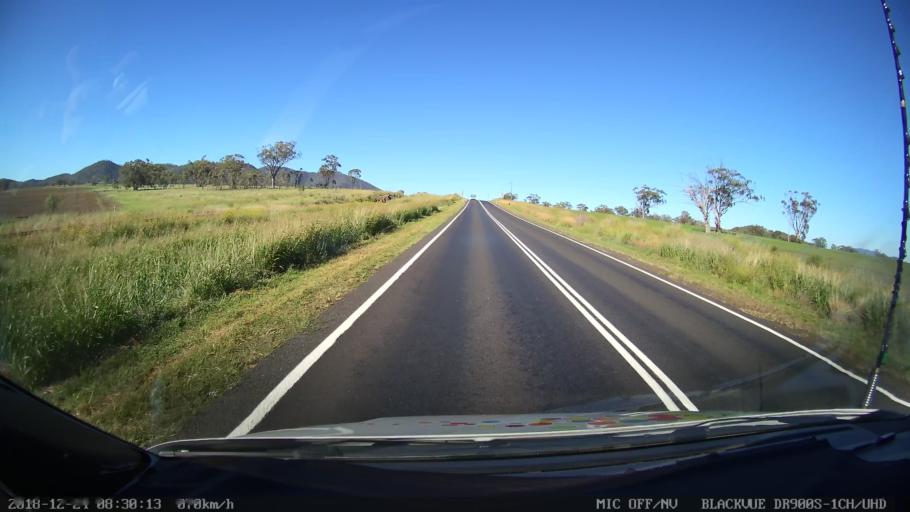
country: AU
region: New South Wales
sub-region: Tamworth Municipality
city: Phillip
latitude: -31.2665
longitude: 150.7269
